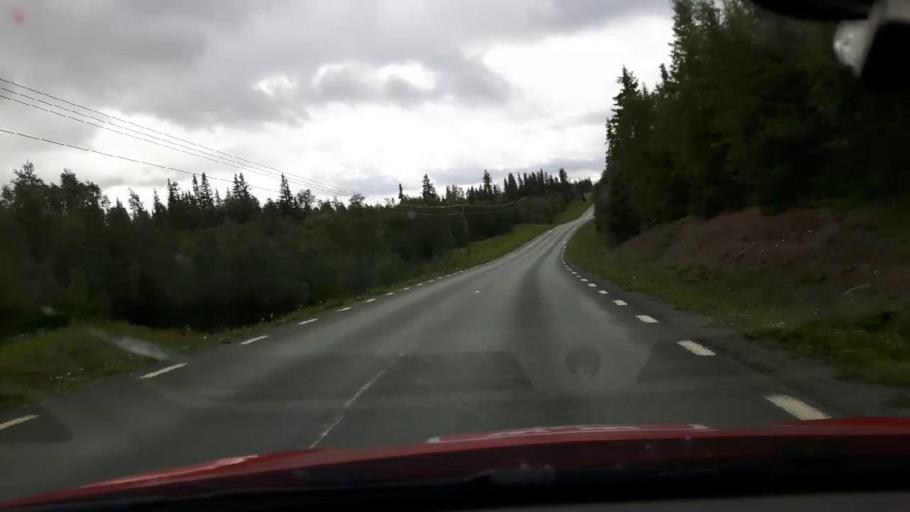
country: SE
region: Jaemtland
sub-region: Are Kommun
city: Are
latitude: 63.3780
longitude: 12.7311
